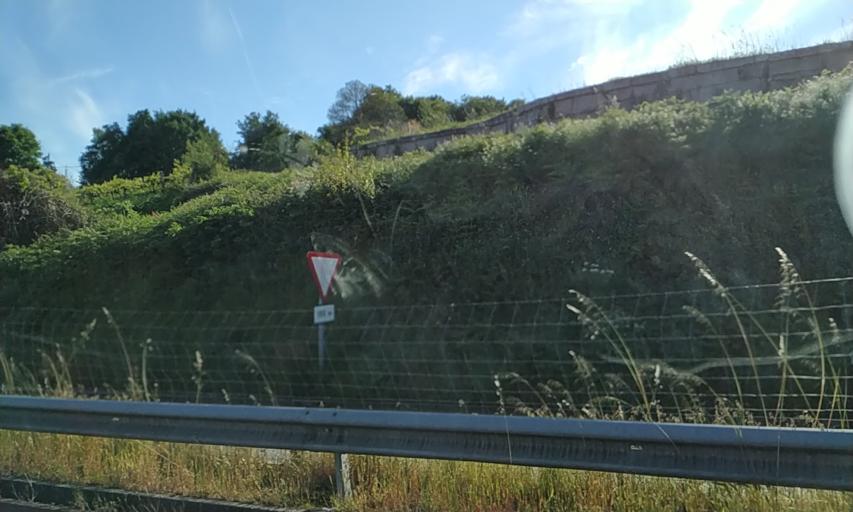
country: ES
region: Galicia
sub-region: Provincia de Pontevedra
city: Porrino
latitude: 42.1856
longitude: -8.6361
